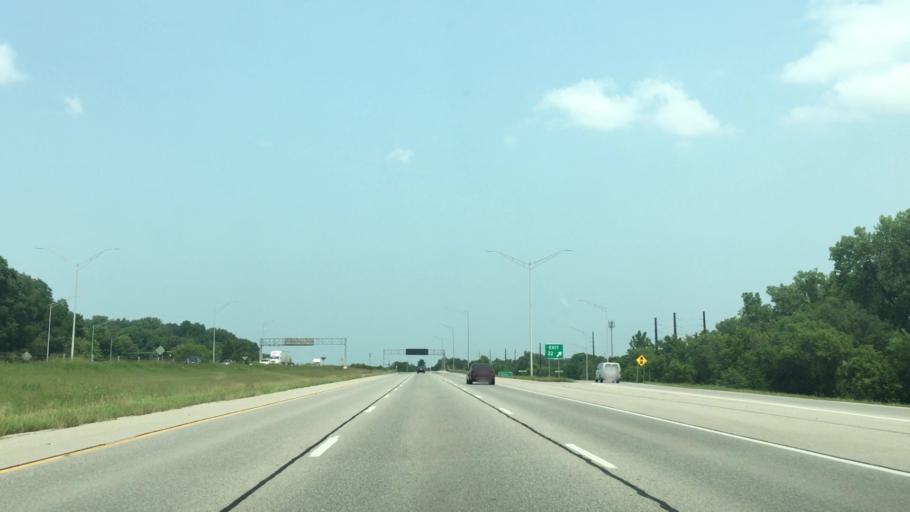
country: US
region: Iowa
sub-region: Linn County
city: Cedar Rapids
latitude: 42.0039
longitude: -91.6662
